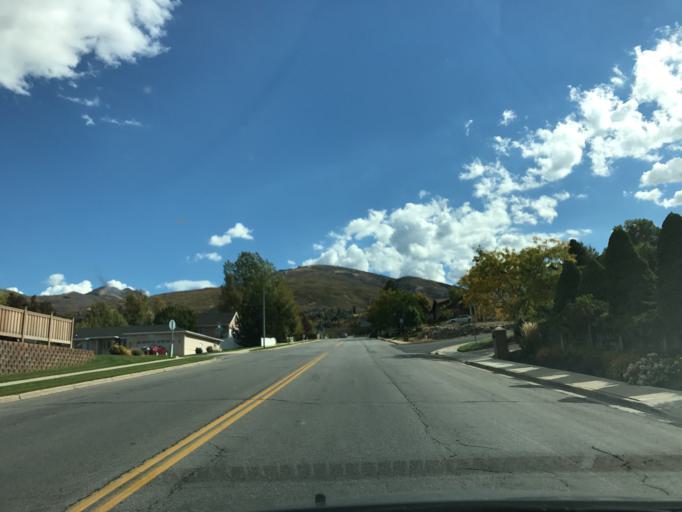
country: US
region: Utah
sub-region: Davis County
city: Bountiful
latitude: 40.8712
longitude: -111.8560
